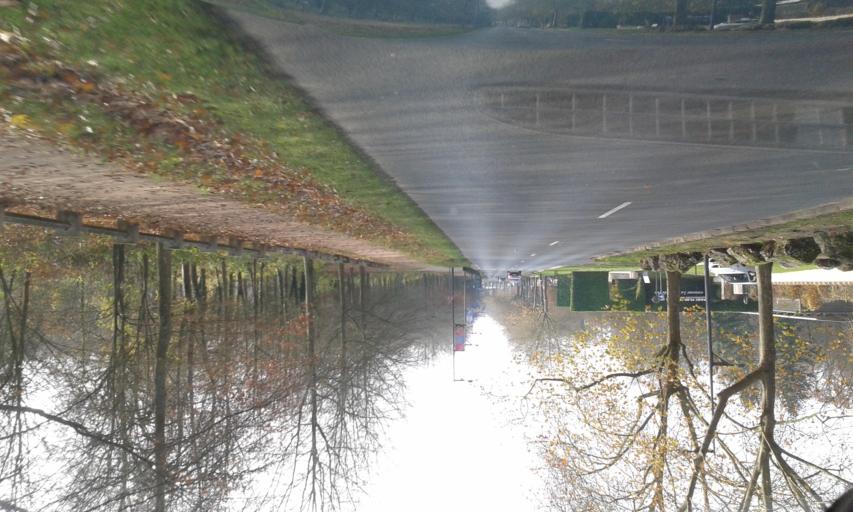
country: FR
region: Centre
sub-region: Departement du Loiret
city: Saint-Cyr-en-Val
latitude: 47.8478
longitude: 1.9362
